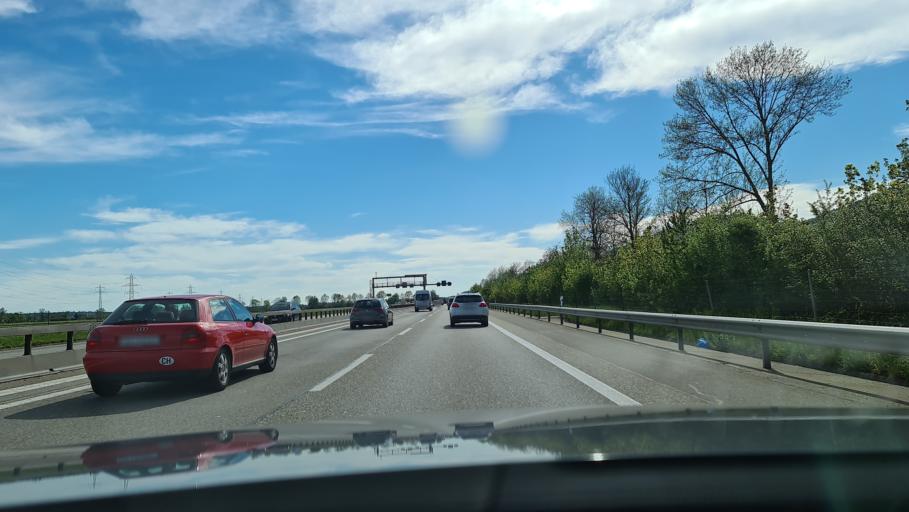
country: CH
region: Solothurn
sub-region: Bezirk Gaeu
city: Oberbuchsiten
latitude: 47.2993
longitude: 7.7613
